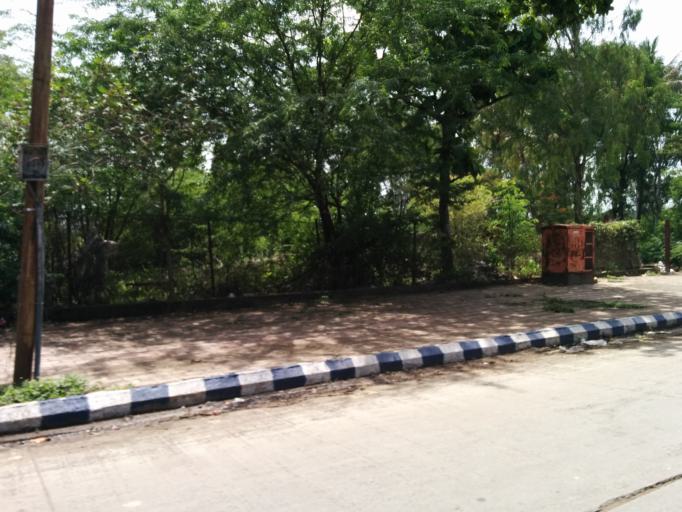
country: IN
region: Maharashtra
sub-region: Pune Division
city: Pune
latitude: 18.5345
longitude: 73.9133
